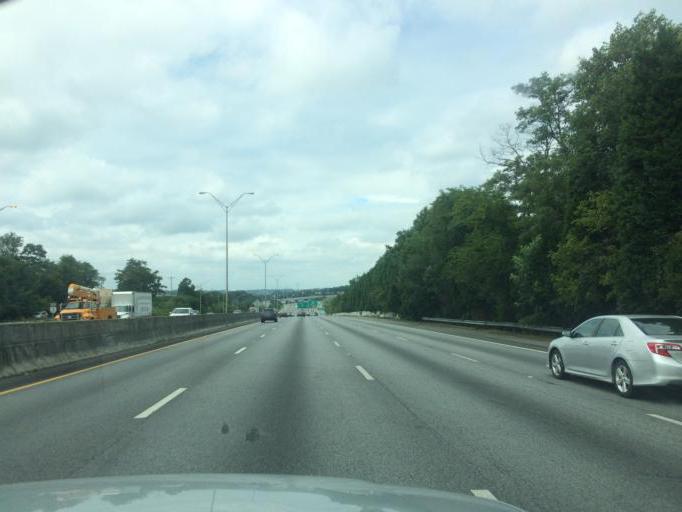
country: US
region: South Carolina
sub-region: Greenville County
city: Mauldin
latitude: 34.8028
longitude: -82.3561
